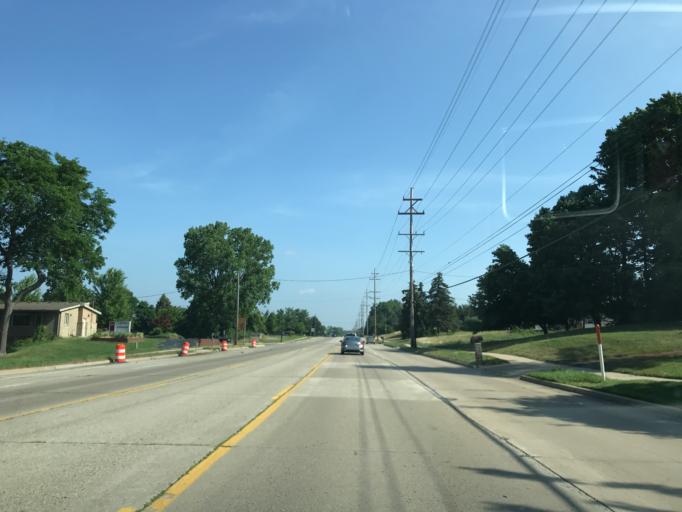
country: US
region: Michigan
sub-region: Ingham County
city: Okemos
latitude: 42.6923
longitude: -84.4323
